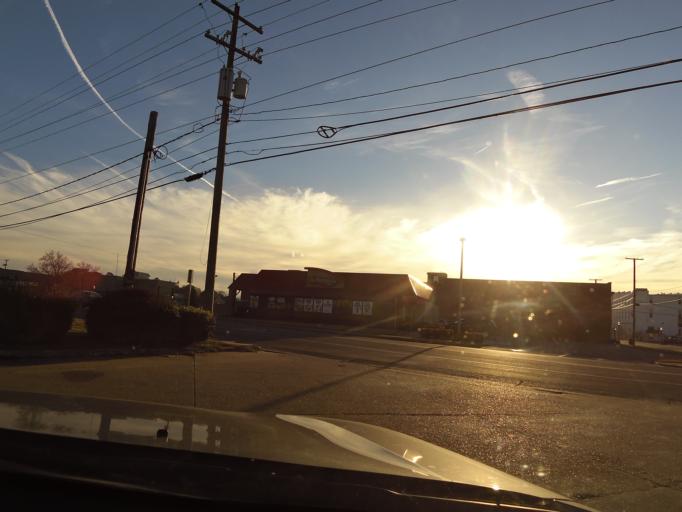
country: US
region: Virginia
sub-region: City of Franklin
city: Franklin
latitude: 36.6786
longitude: -76.9209
